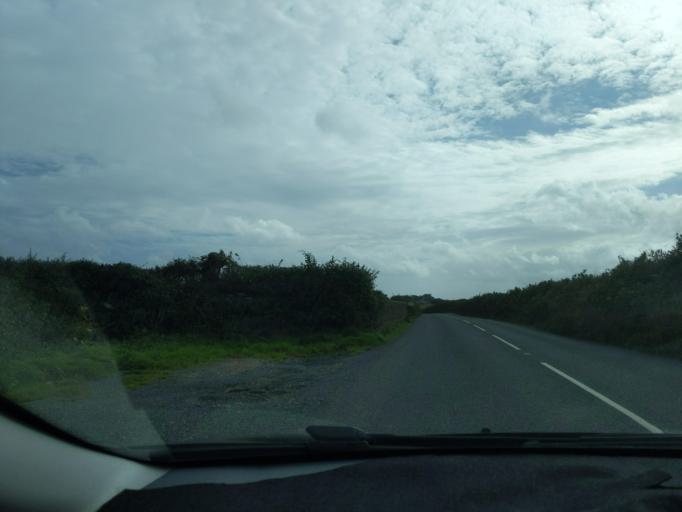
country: GB
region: England
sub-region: Cornwall
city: Mevagissey
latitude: 50.2769
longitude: -4.8297
